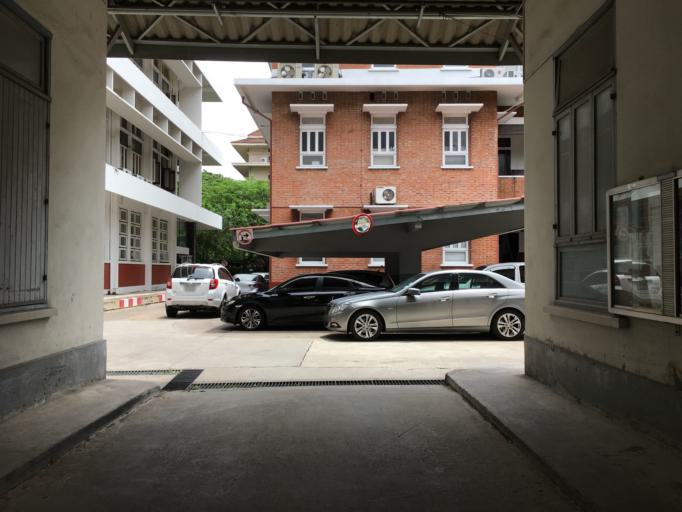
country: TH
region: Bangkok
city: Pathum Wan
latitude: 13.7363
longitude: 100.5324
